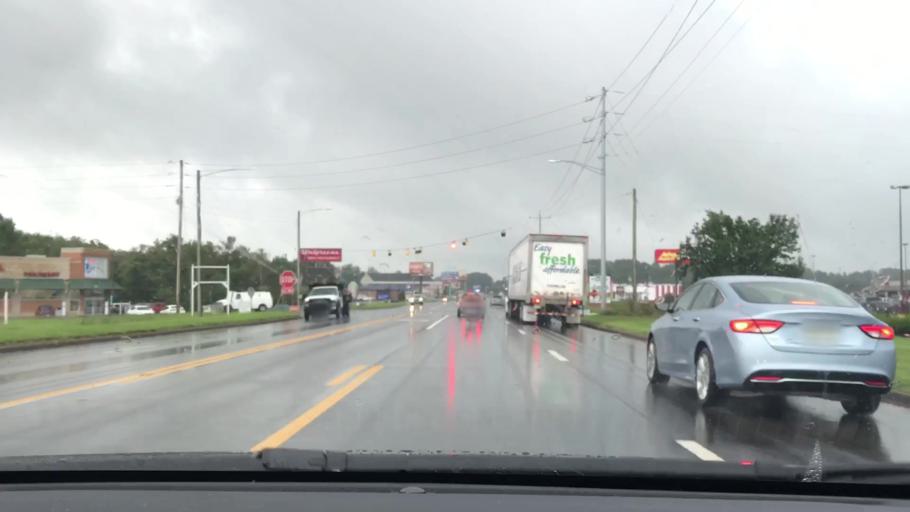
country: US
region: Tennessee
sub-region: Macon County
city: Lafayette
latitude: 36.5228
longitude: -86.0394
